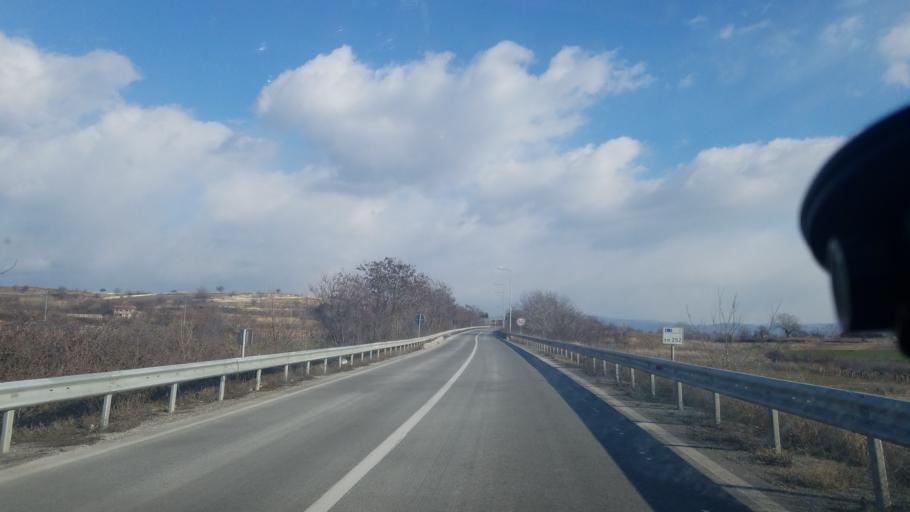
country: MK
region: Kocani
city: Orizari
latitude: 41.9101
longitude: 22.4507
